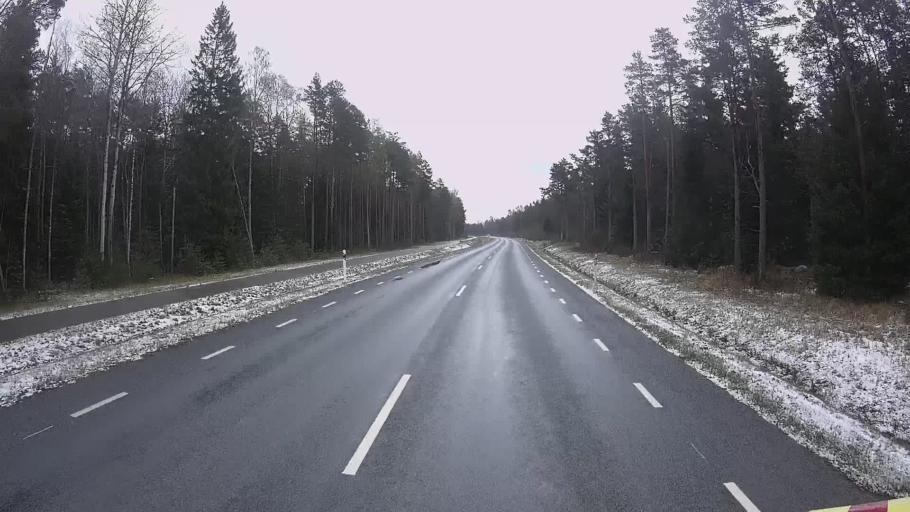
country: EE
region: Hiiumaa
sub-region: Kaerdla linn
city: Kardla
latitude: 59.0091
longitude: 22.6805
